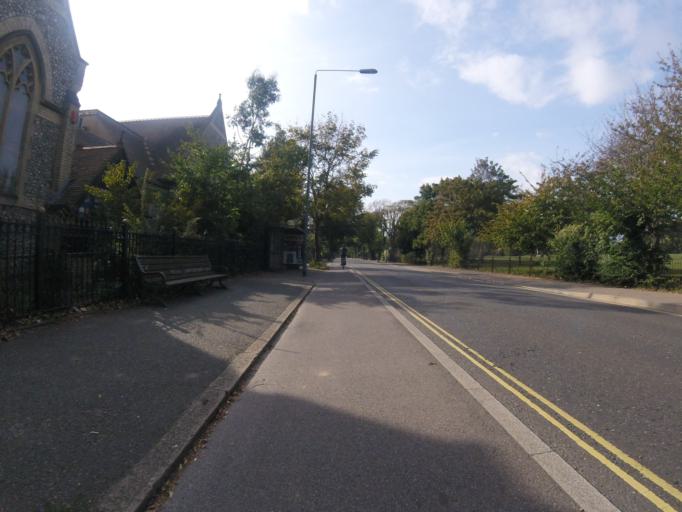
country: GB
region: England
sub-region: Brighton and Hove
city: Hove
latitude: 50.8344
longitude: -0.1547
